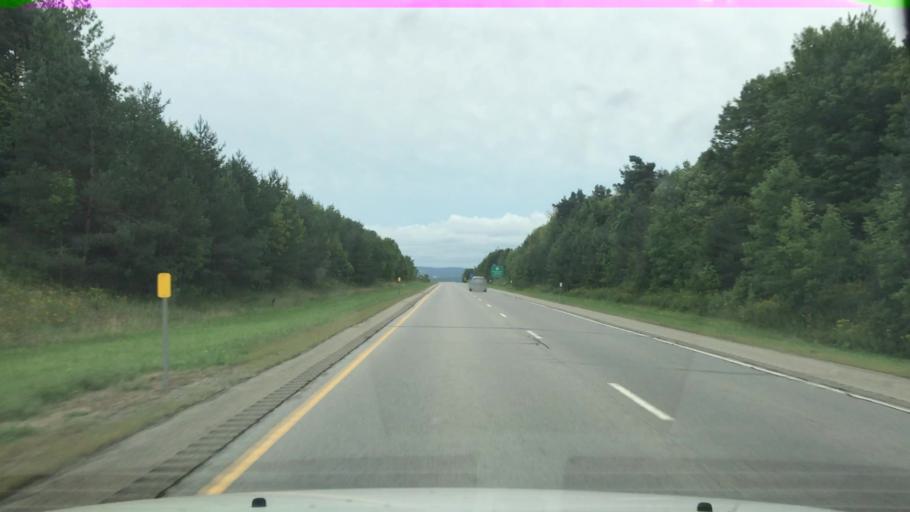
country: US
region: New York
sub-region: Erie County
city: Springville
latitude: 42.5302
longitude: -78.7034
